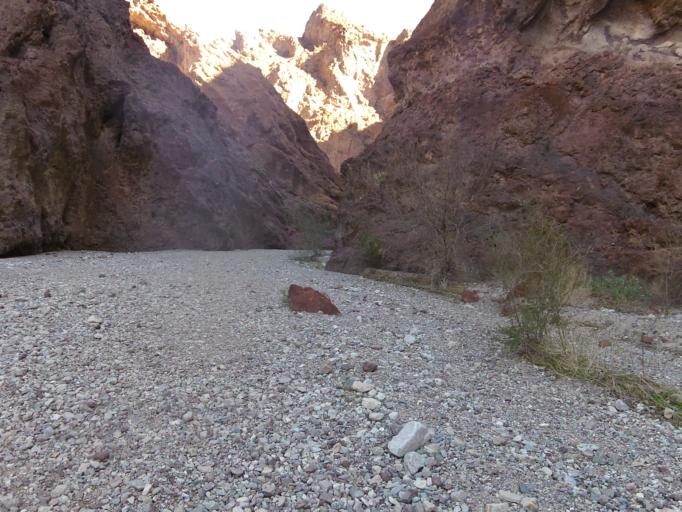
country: US
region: Nevada
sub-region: Clark County
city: Boulder City
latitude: 35.9638
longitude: -114.7281
